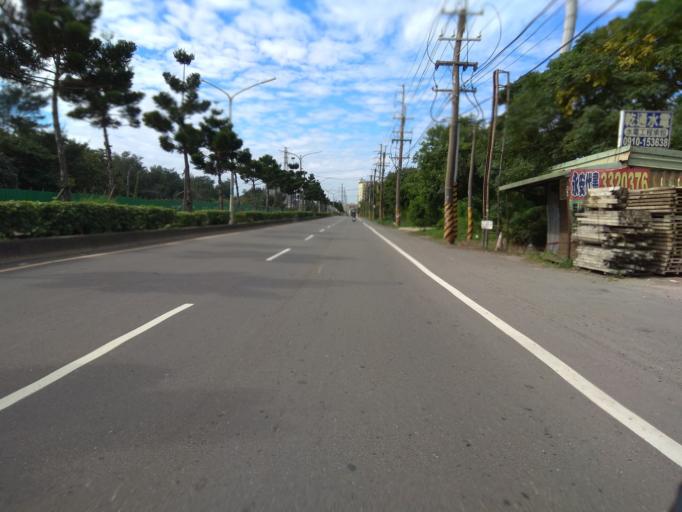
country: TW
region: Taiwan
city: Taoyuan City
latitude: 25.0551
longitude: 121.1373
